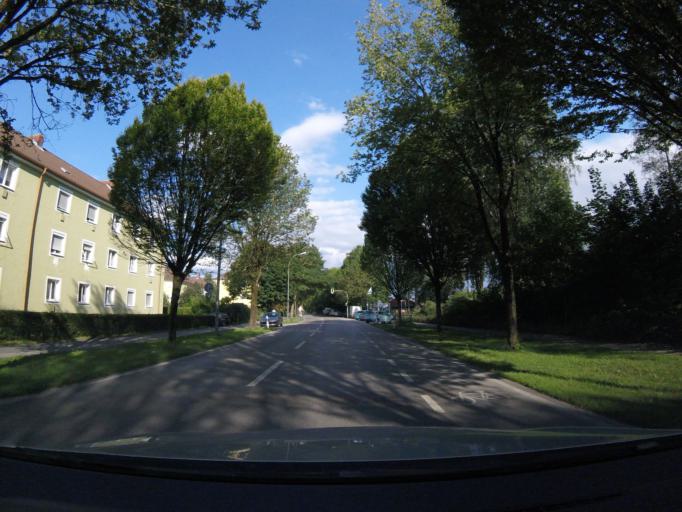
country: DE
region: Bavaria
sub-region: Upper Bavaria
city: Bogenhausen
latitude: 48.1326
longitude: 11.6357
